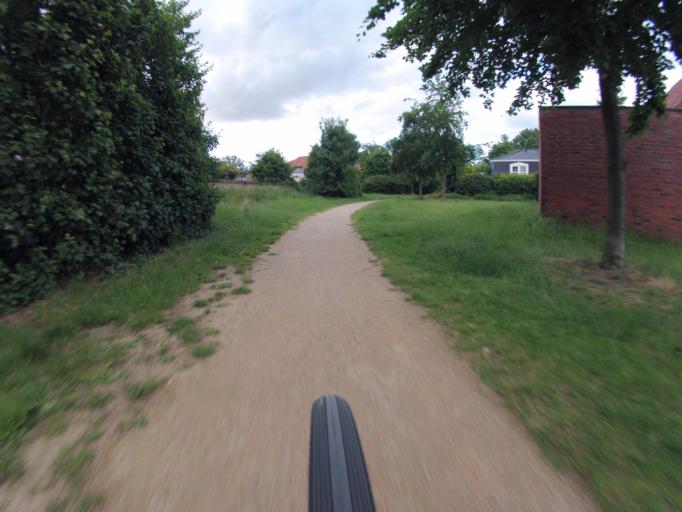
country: DE
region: North Rhine-Westphalia
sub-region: Regierungsbezirk Munster
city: Birgte
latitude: 52.2971
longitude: 7.6497
